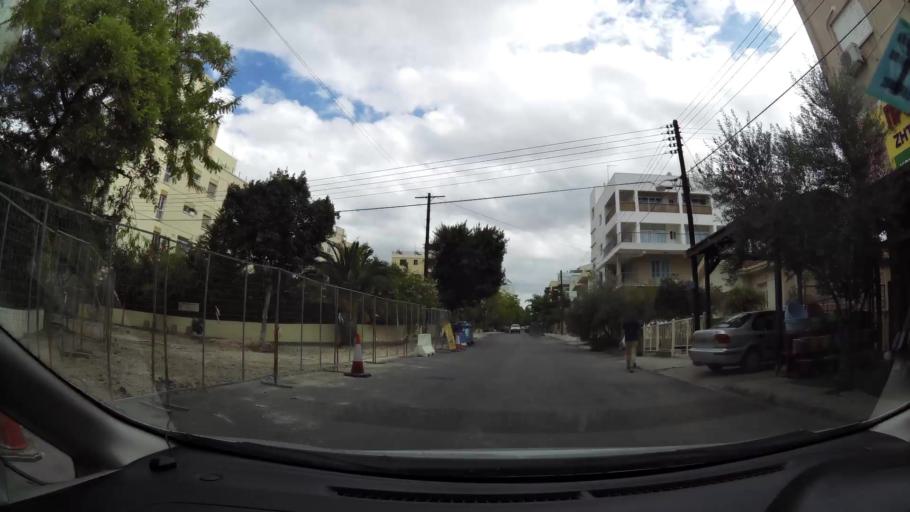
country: CY
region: Lefkosia
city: Nicosia
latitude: 35.1563
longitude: 33.3590
